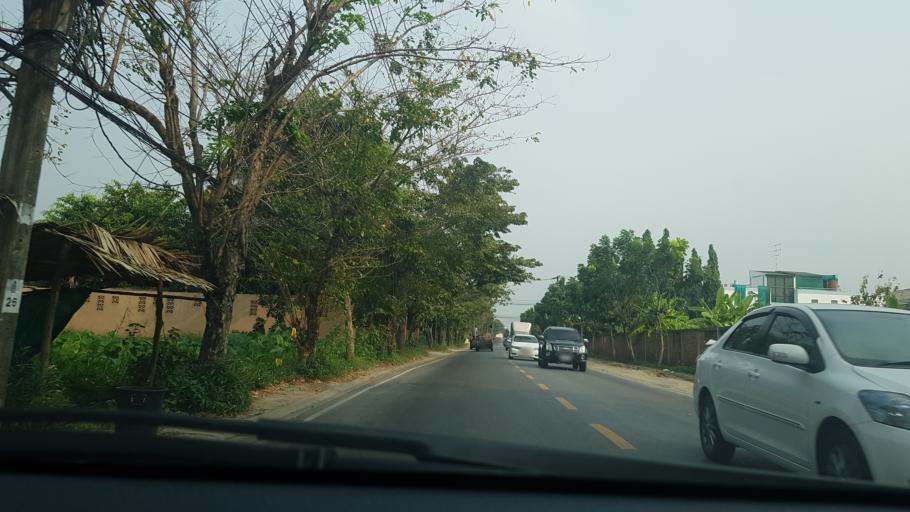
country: TH
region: Bangkok
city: Phasi Charoen
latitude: 13.7563
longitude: 100.3970
